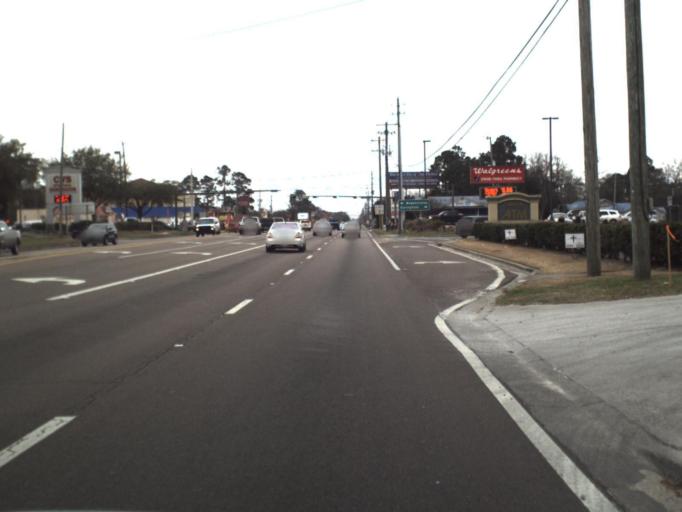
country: US
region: Florida
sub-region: Bay County
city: Springfield
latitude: 30.1545
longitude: -85.5912
